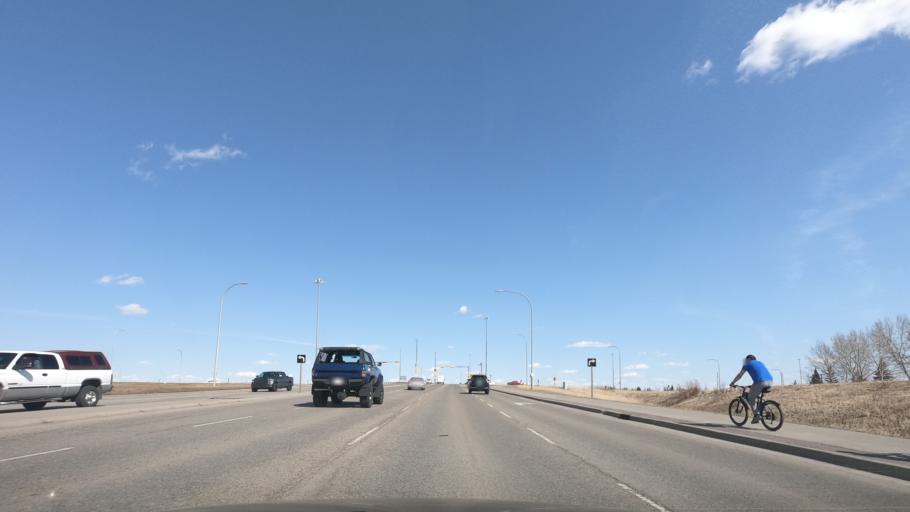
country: CA
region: Alberta
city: Airdrie
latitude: 51.2999
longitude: -114.0060
